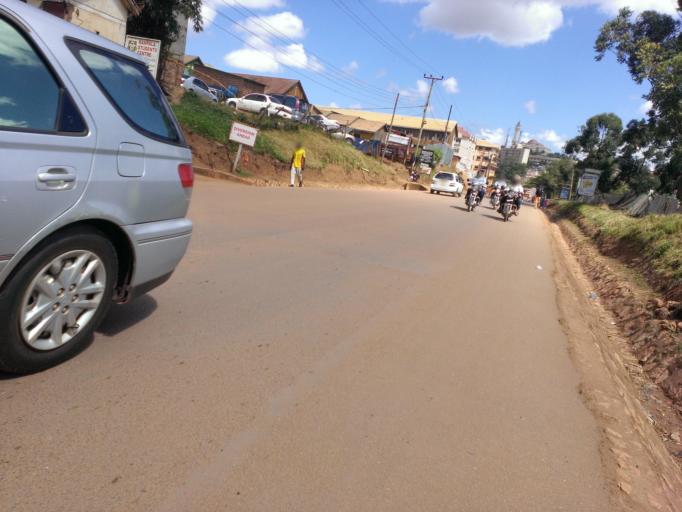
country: UG
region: Central Region
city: Kampala Central Division
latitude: 0.3242
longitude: 32.5697
